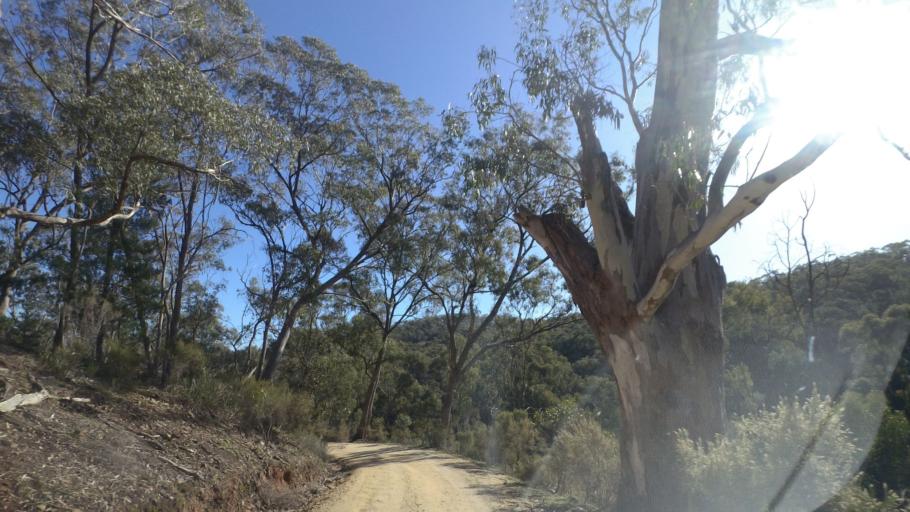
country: AU
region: Victoria
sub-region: Mount Alexander
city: Castlemaine
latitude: -37.0320
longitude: 144.2697
